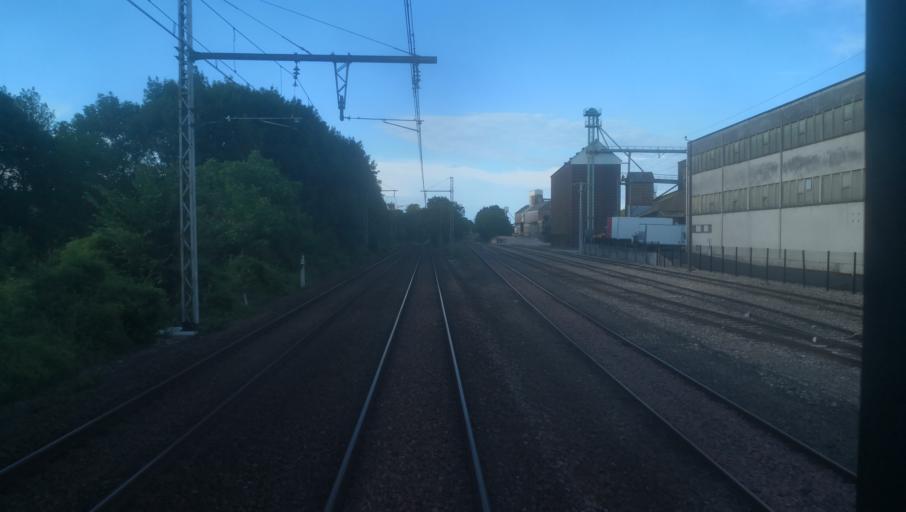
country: FR
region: Centre
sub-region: Departement de l'Indre
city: Issoudun
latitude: 46.9661
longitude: 1.9992
